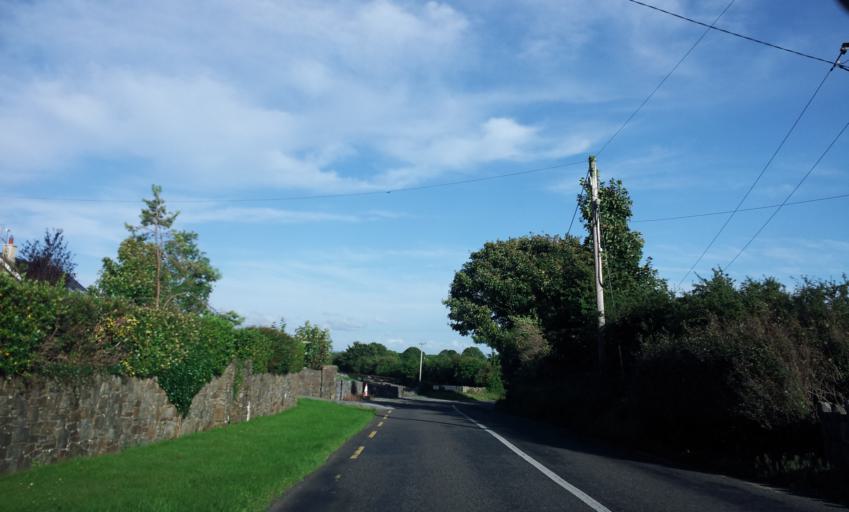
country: IE
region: Munster
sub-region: An Clar
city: Ennis
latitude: 52.9723
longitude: -9.0901
